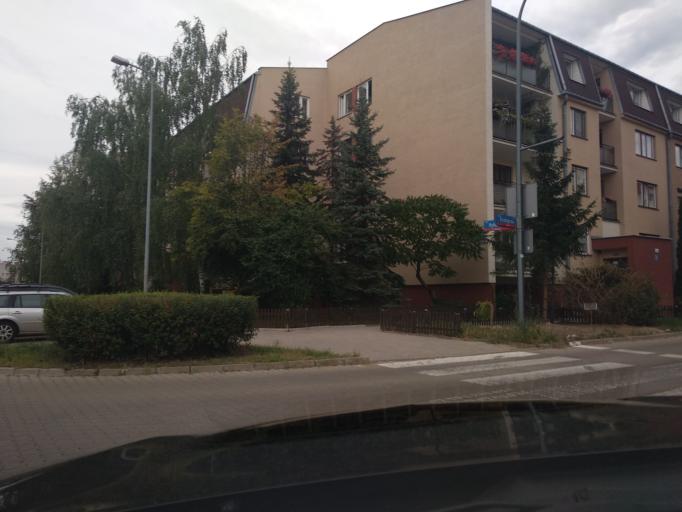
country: PL
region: Masovian Voivodeship
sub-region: Warszawa
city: Ursynow
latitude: 52.1297
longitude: 21.0559
